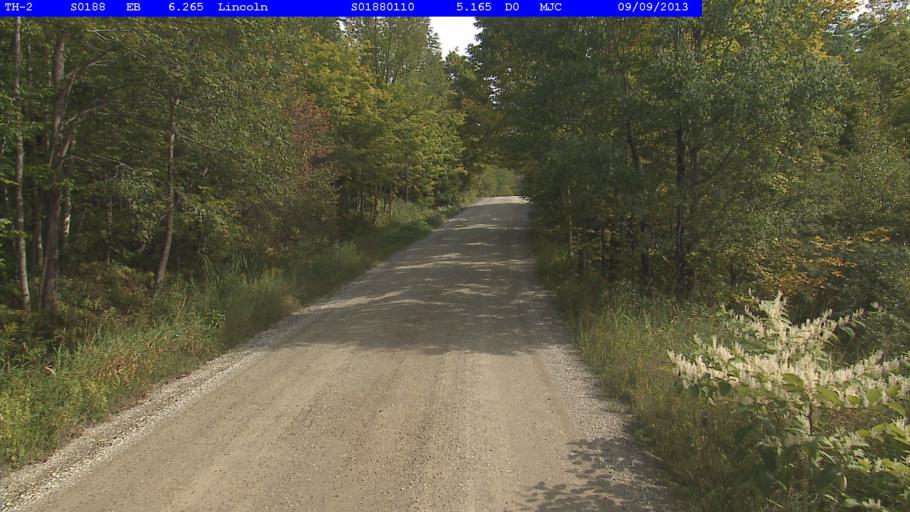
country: US
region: Vermont
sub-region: Addison County
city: Bristol
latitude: 44.0904
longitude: -72.9512
